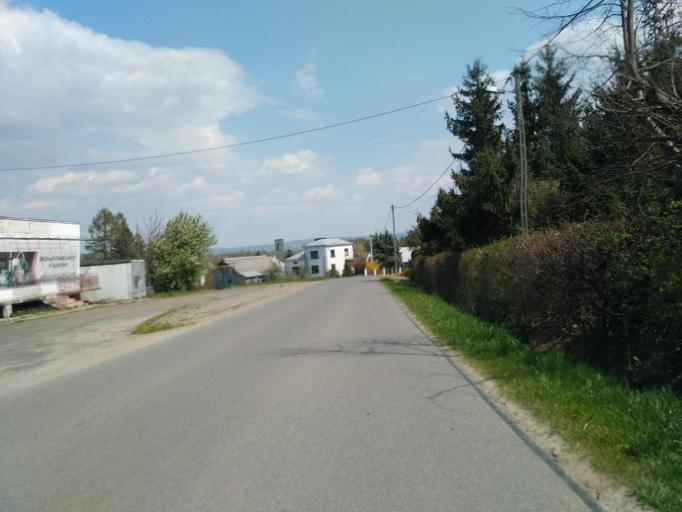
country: PL
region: Subcarpathian Voivodeship
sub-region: Powiat jasielski
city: Tarnowiec
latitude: 49.7437
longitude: 21.5791
